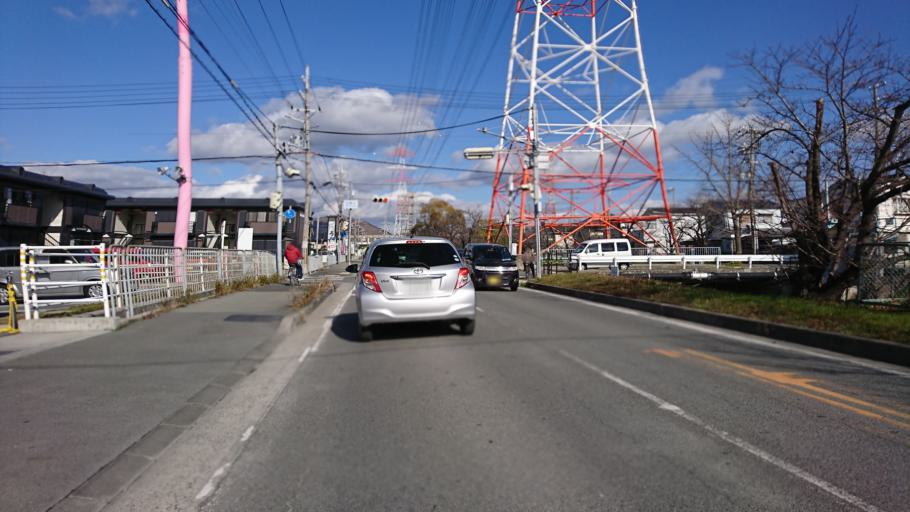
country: JP
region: Hyogo
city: Kakogawacho-honmachi
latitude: 34.7788
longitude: 134.7798
